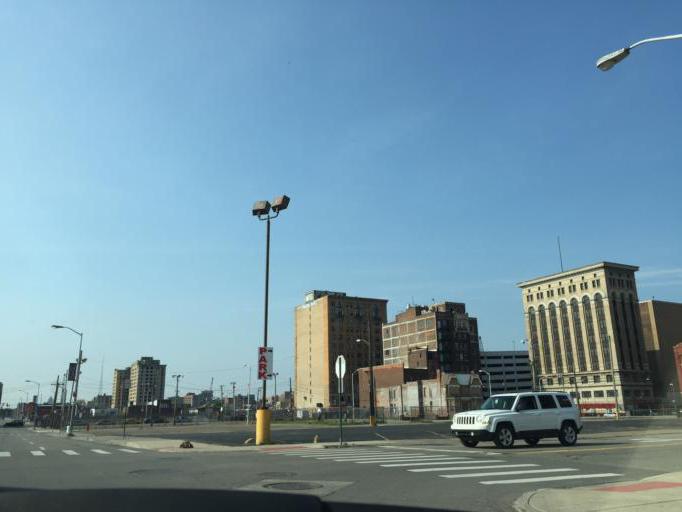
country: US
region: Michigan
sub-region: Wayne County
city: Detroit
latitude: 42.3363
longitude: -83.0542
